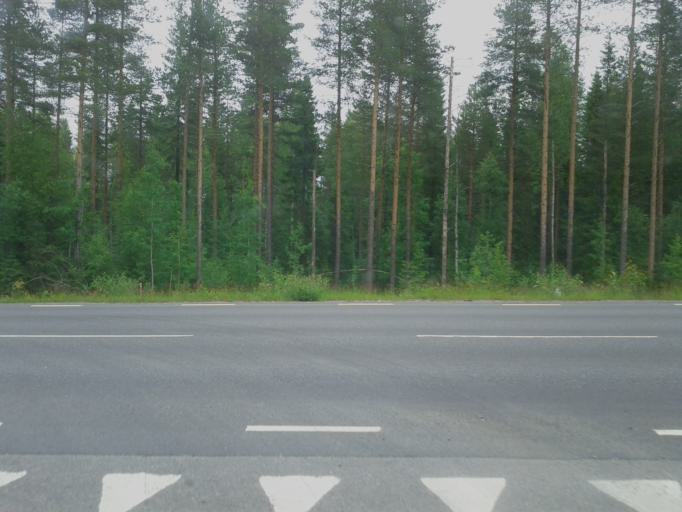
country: SE
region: Vaesterbotten
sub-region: Skelleftea Kommun
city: Boliden
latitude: 64.8719
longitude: 20.3885
